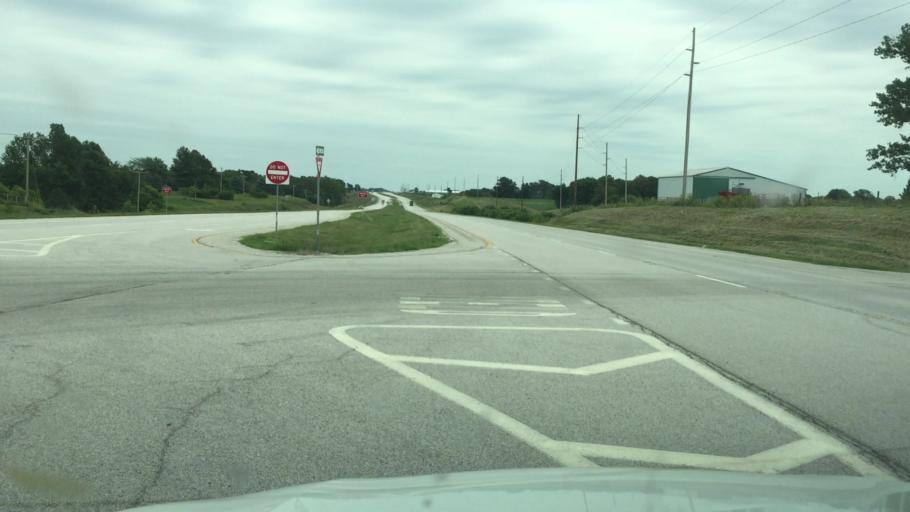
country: US
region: Illinois
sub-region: Hancock County
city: Carthage
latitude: 40.4153
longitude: -91.0823
